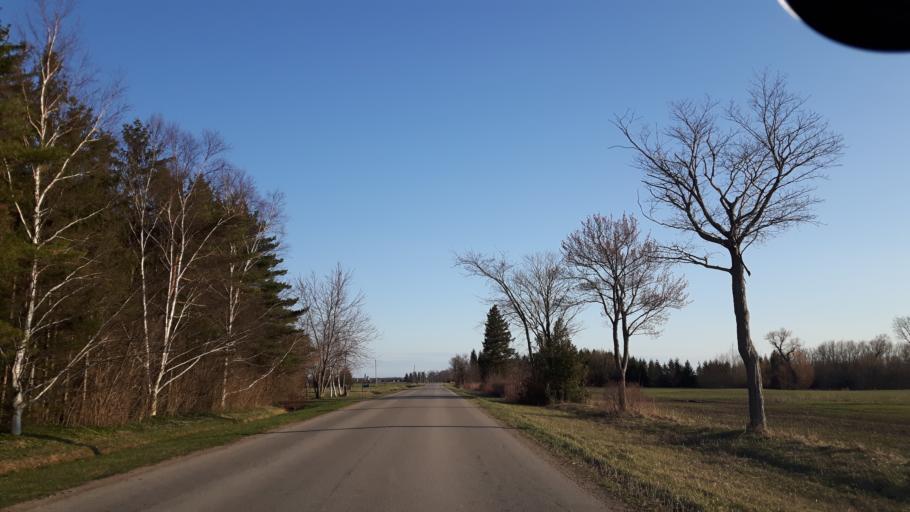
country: CA
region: Ontario
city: Goderich
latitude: 43.6527
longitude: -81.6846
